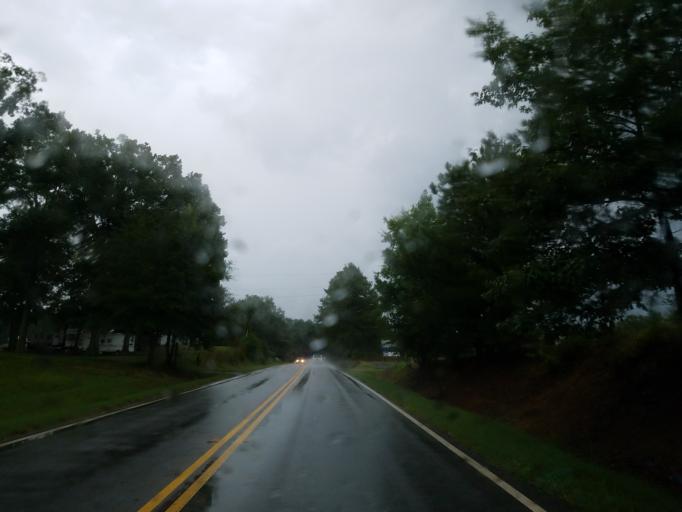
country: US
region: Georgia
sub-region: Floyd County
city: Shannon
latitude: 34.3841
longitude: -85.1500
